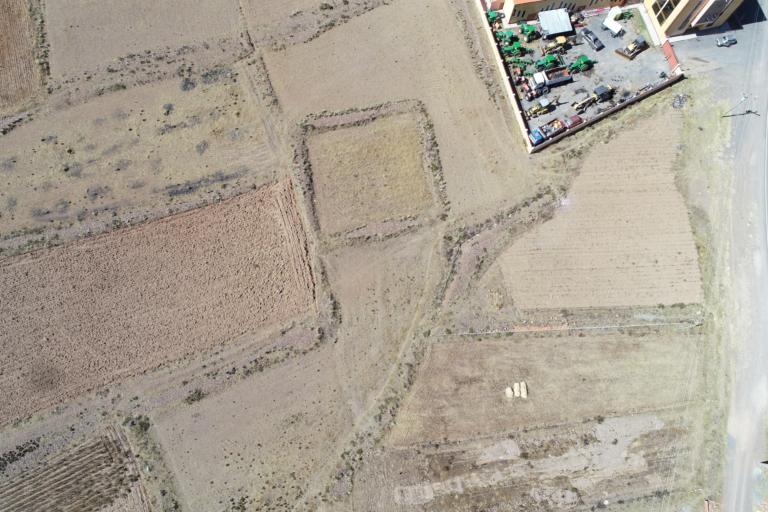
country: BO
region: La Paz
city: Achacachi
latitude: -15.8992
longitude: -68.9010
